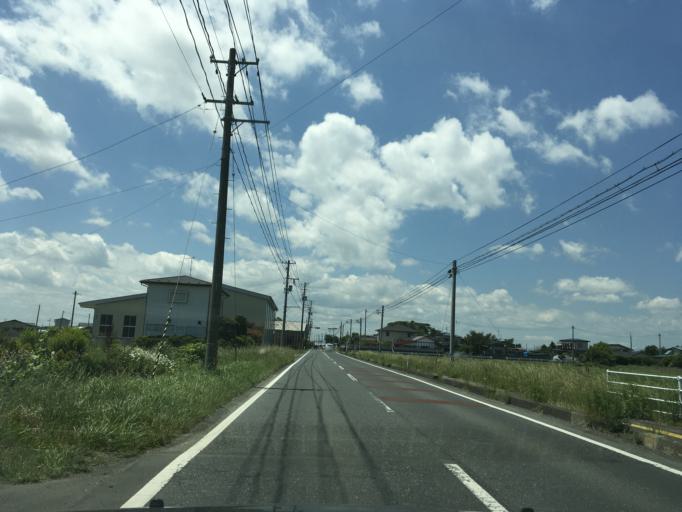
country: JP
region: Miyagi
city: Wakuya
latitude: 38.6765
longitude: 141.2495
